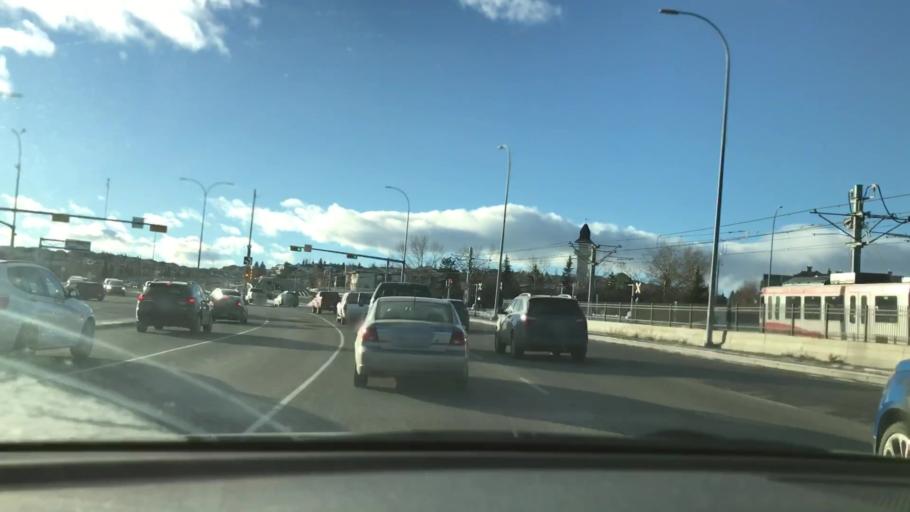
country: CA
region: Alberta
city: Calgary
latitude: 51.0398
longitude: -114.1650
